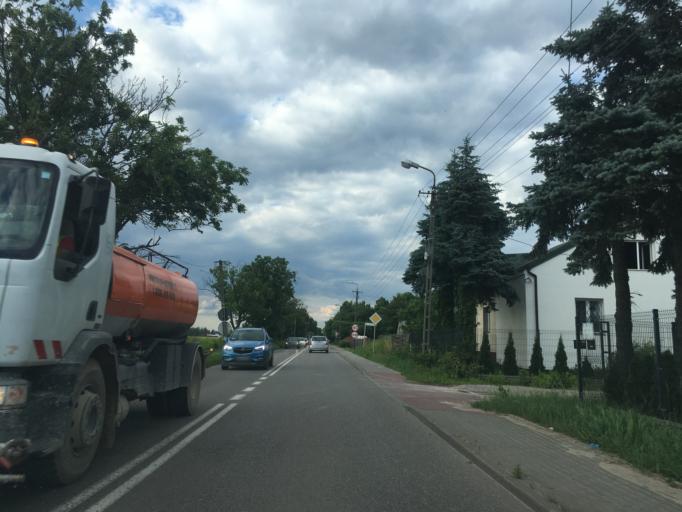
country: PL
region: Masovian Voivodeship
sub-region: Powiat piaseczynski
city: Lesznowola
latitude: 52.0944
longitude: 20.9729
